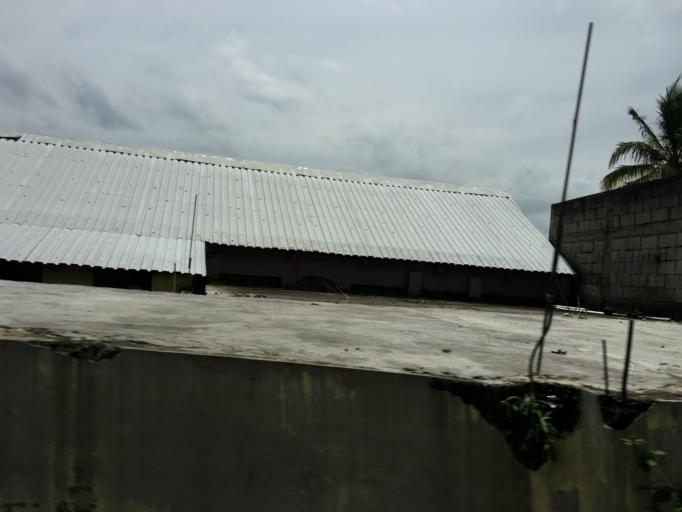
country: GT
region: Guatemala
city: Villa Canales
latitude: 14.4407
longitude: -90.5591
